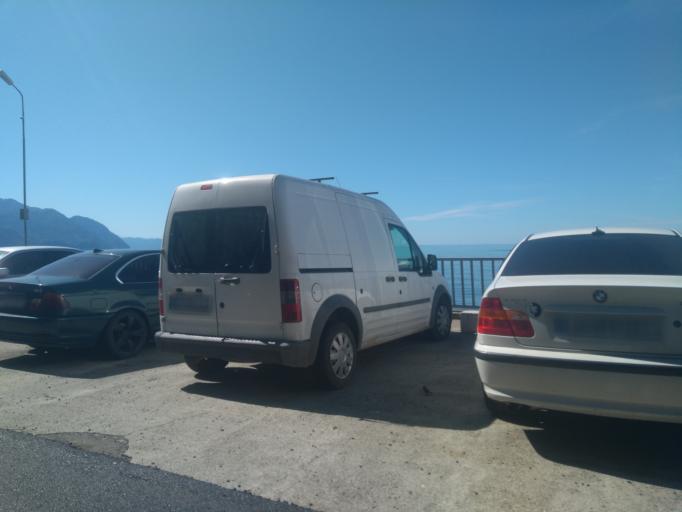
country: TR
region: Artvin
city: Kemalpasa
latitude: 41.5253
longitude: 41.5490
